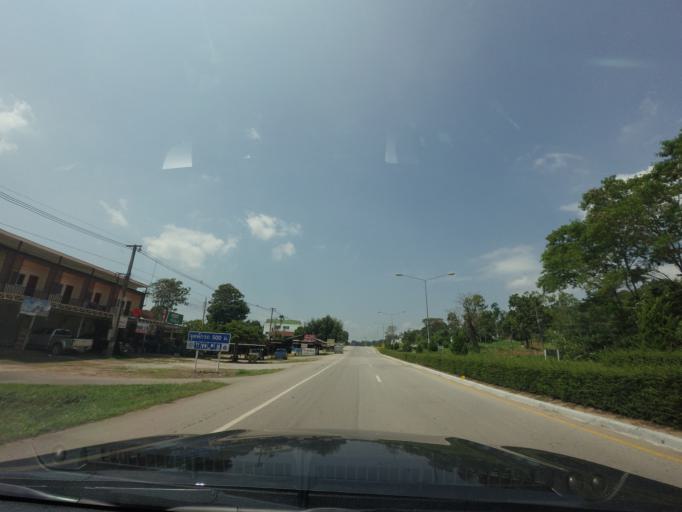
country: TH
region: Loei
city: Phu Ruea
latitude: 17.4571
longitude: 101.3719
